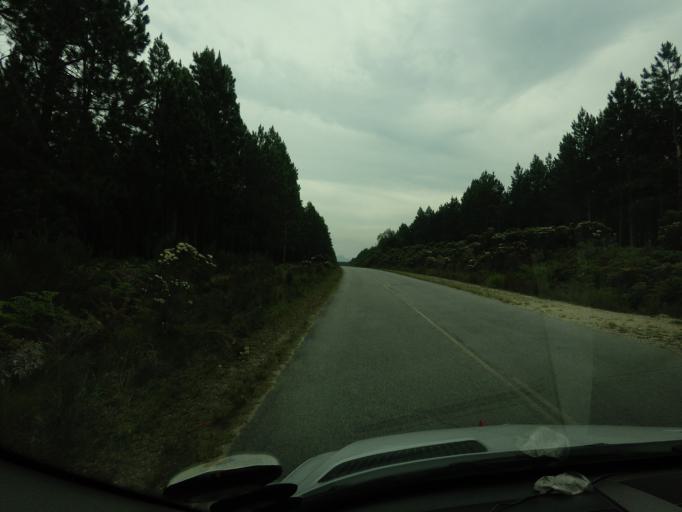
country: ZA
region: Eastern Cape
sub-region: Cacadu District Municipality
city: Kareedouw
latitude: -33.9959
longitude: 23.8520
